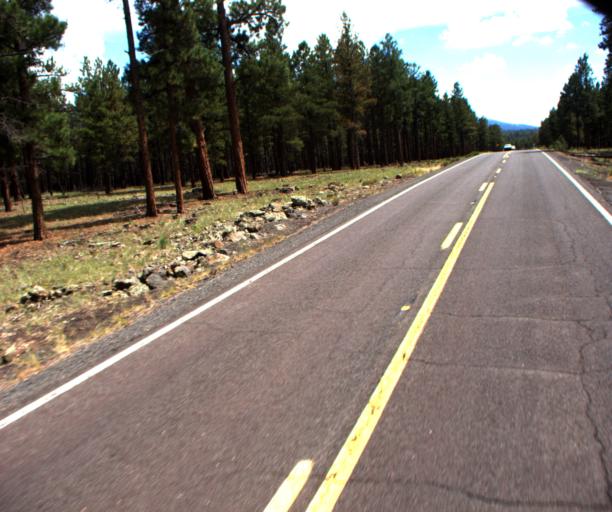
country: US
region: Arizona
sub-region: Coconino County
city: Parks
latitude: 35.4558
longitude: -111.7758
